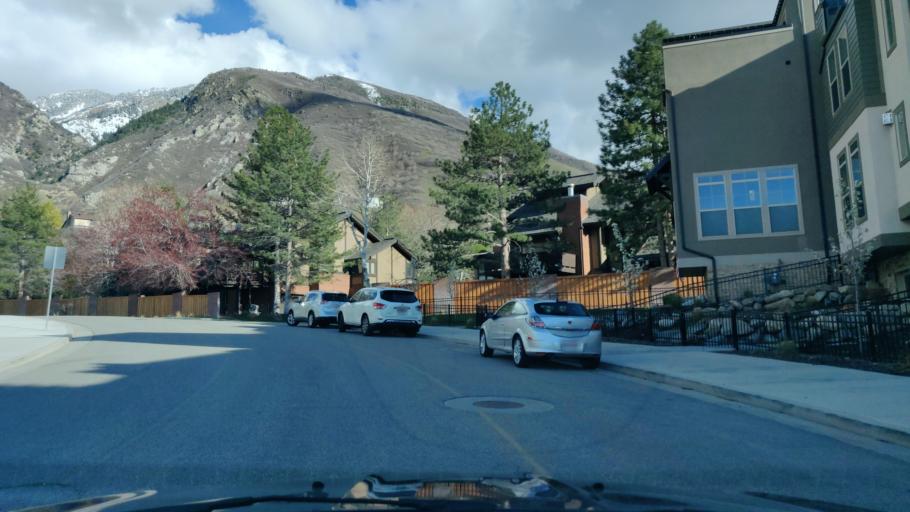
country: US
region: Utah
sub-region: Salt Lake County
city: Cottonwood Heights
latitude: 40.6168
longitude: -111.7905
